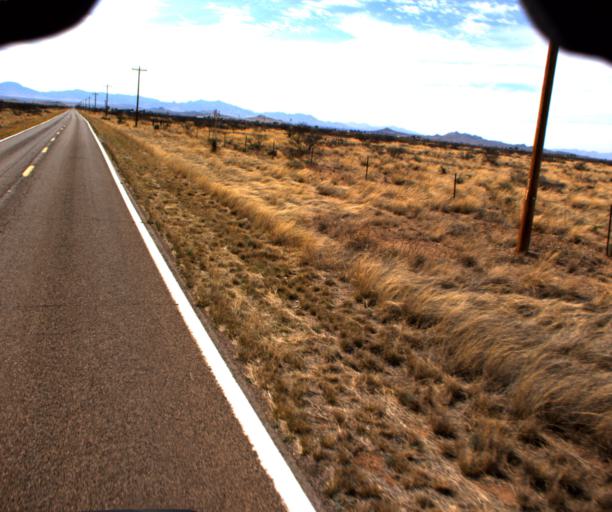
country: US
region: Arizona
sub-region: Cochise County
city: Willcox
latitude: 31.8762
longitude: -109.5921
